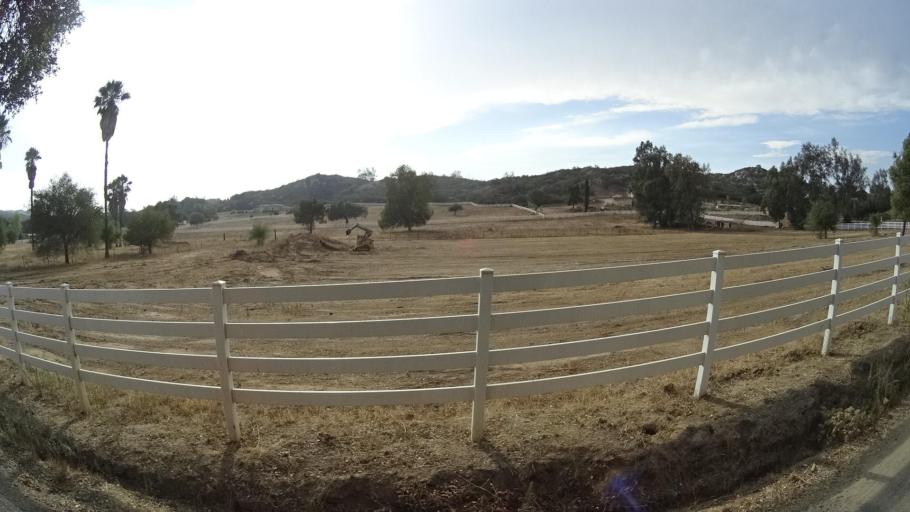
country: US
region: California
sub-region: San Diego County
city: Lakeside
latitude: 32.9220
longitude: -116.8841
